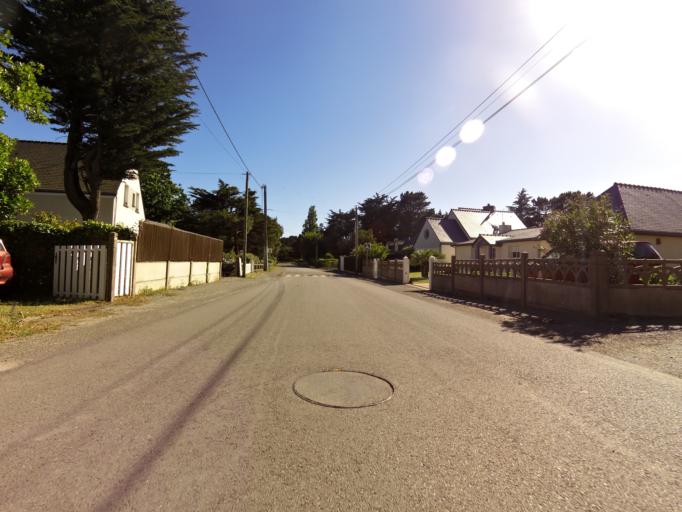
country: FR
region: Brittany
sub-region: Departement du Morbihan
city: Penestin
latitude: 47.4689
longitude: -2.4868
